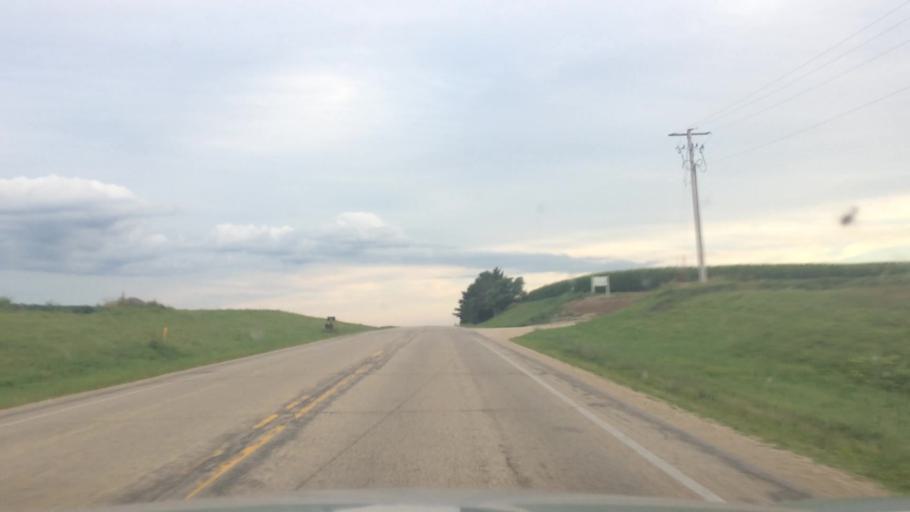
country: US
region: Wisconsin
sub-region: Columbia County
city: Lodi
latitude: 43.2438
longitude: -89.5210
